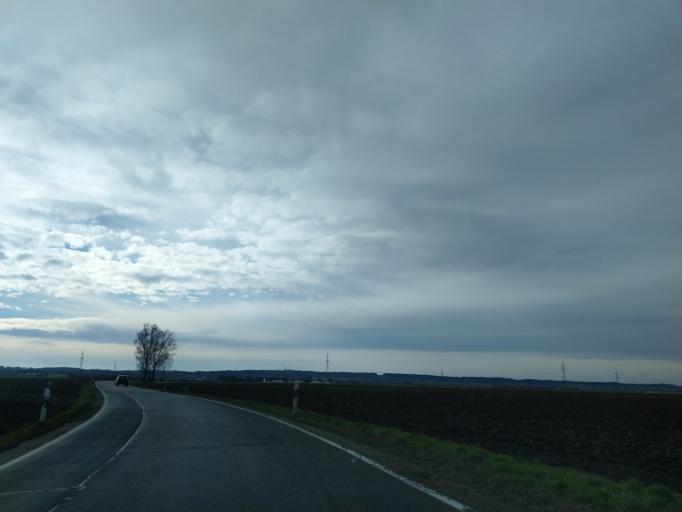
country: DE
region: Bavaria
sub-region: Lower Bavaria
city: Osterhofen
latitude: 48.6842
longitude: 13.0056
